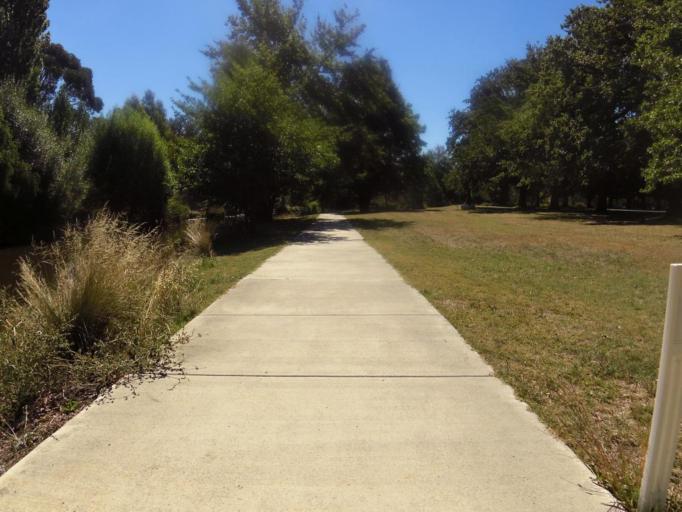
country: AU
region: Victoria
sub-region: Mount Alexander
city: Castlemaine
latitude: -37.2429
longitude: 144.4414
